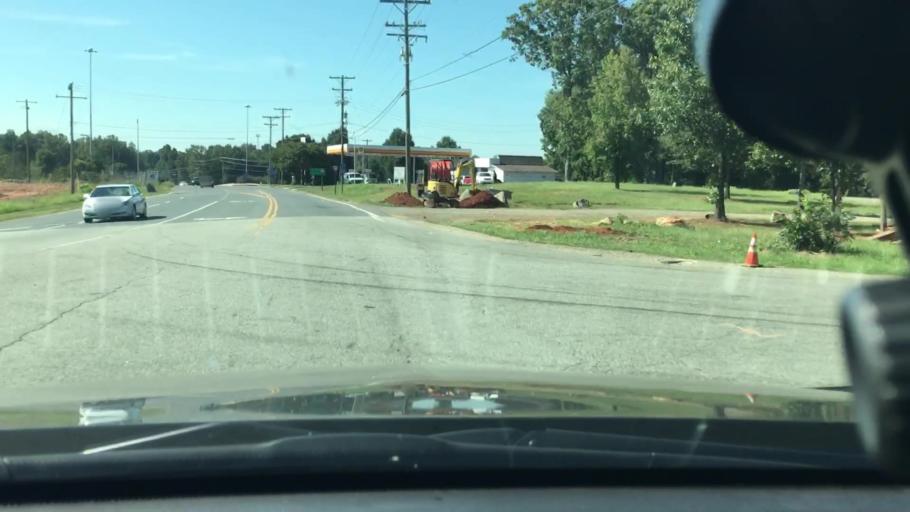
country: US
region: North Carolina
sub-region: Gaston County
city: Mount Holly
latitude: 35.2566
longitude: -80.9812
